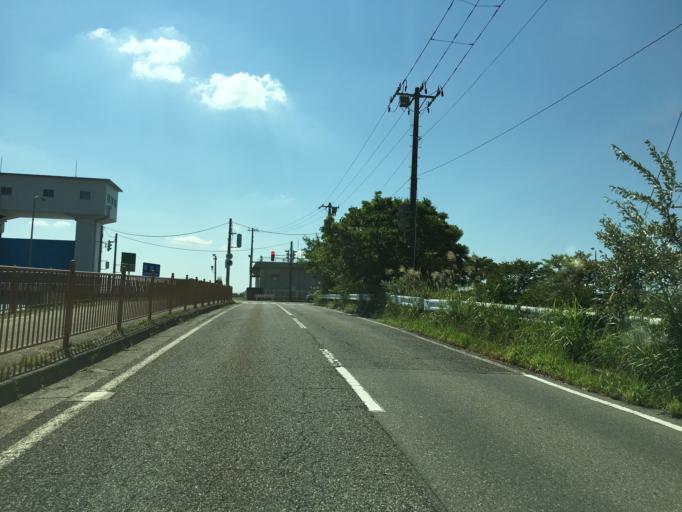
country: JP
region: Niigata
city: Niigata-shi
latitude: 37.8978
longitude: 139.0125
